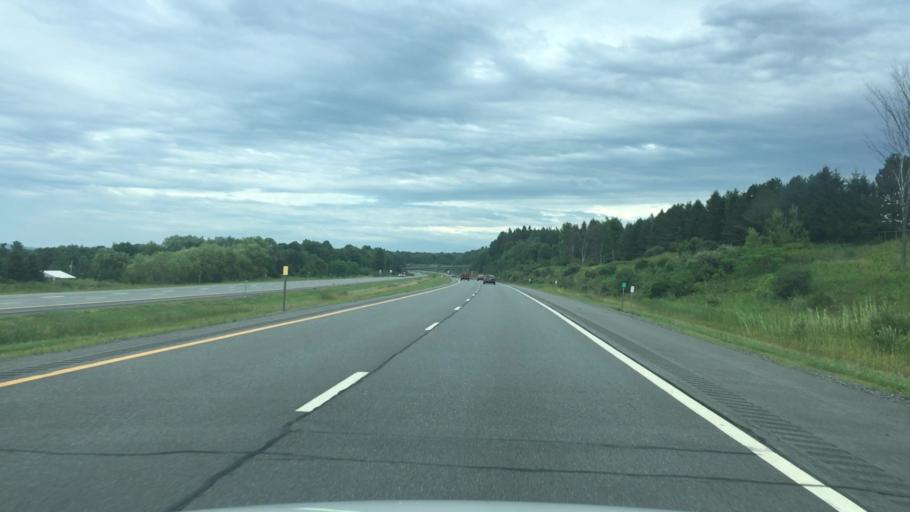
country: US
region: New York
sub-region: Schoharie County
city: Schoharie
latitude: 42.7283
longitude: -74.1950
